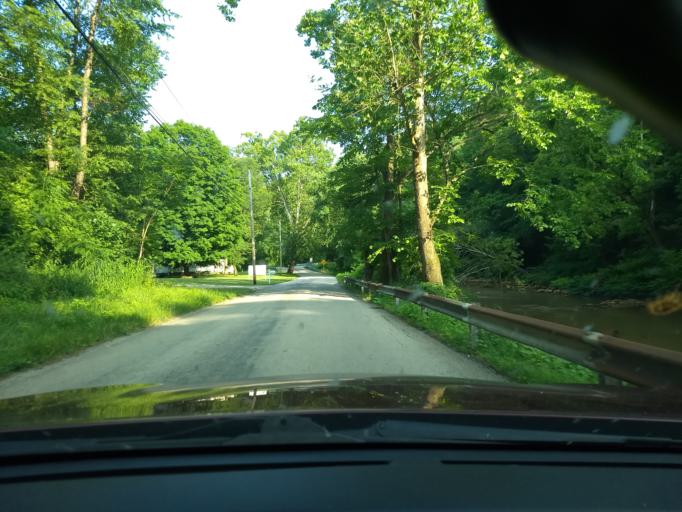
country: US
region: Pennsylvania
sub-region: Westmoreland County
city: Trafford
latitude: 40.3725
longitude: -79.7636
